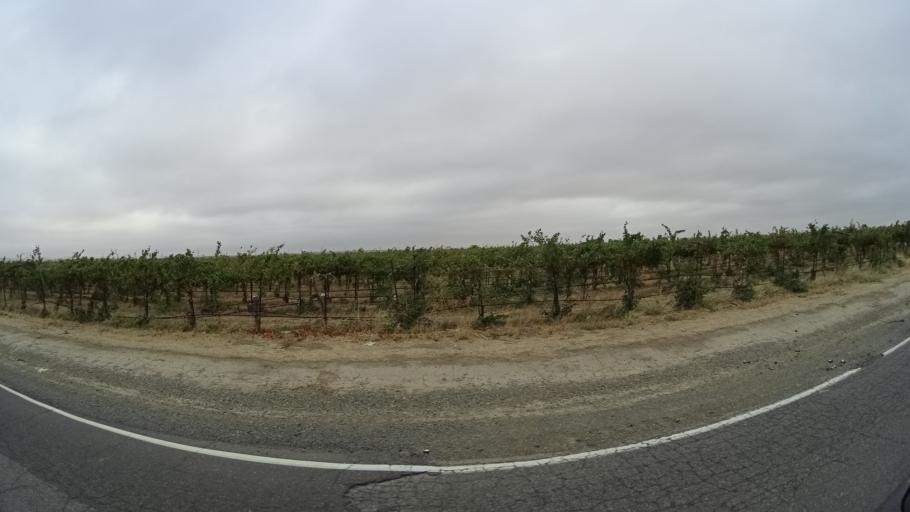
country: US
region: California
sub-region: Yolo County
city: Esparto
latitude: 38.7930
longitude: -122.0437
